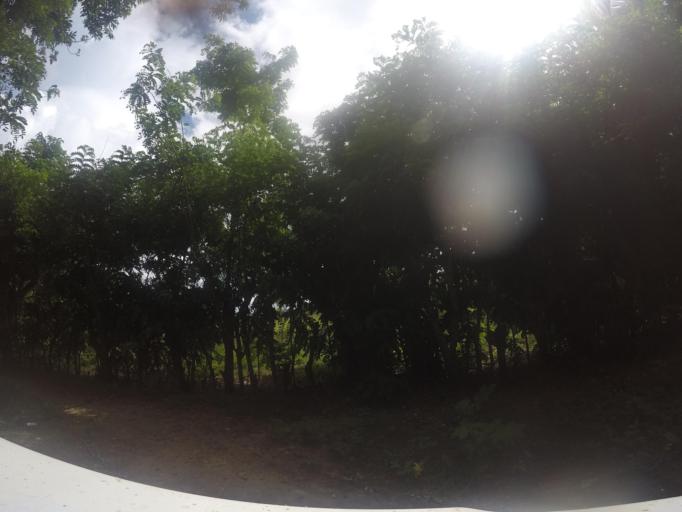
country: TL
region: Lautem
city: Lospalos
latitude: -8.5053
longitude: 127.0079
